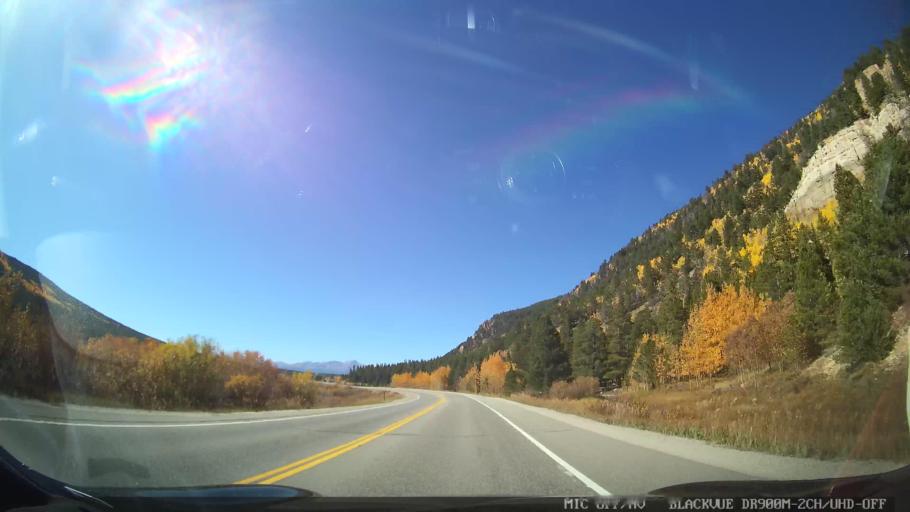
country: US
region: Colorado
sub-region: Lake County
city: Leadville North
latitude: 39.2965
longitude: -106.2726
